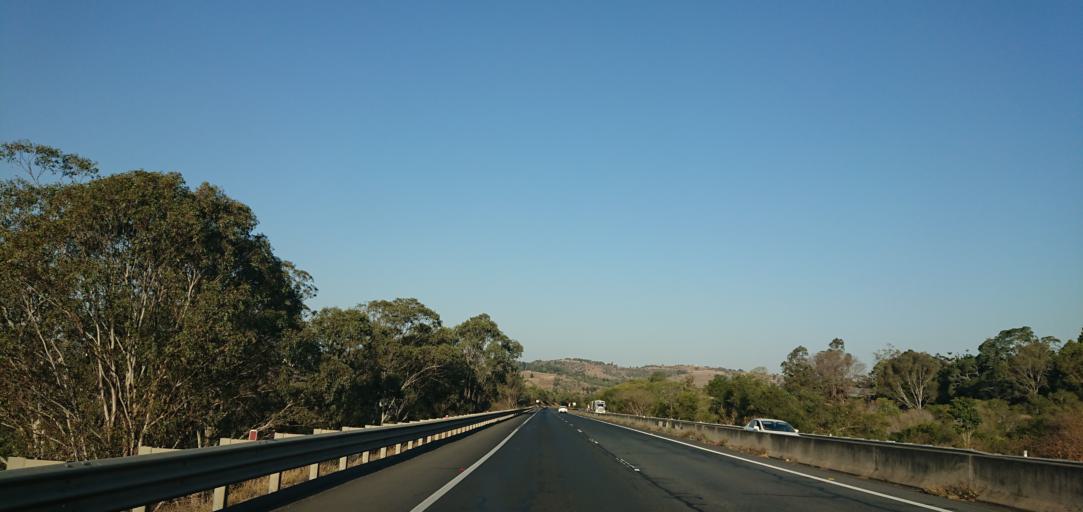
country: AU
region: Queensland
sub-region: Ipswich
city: Thagoona
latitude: -27.5492
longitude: 152.5320
